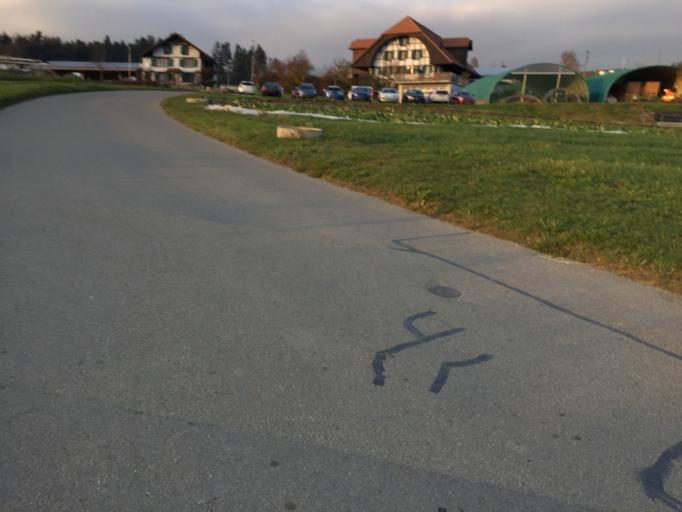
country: CH
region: Bern
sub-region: Bern-Mittelland District
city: Taegertschi
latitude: 46.8793
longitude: 7.5802
